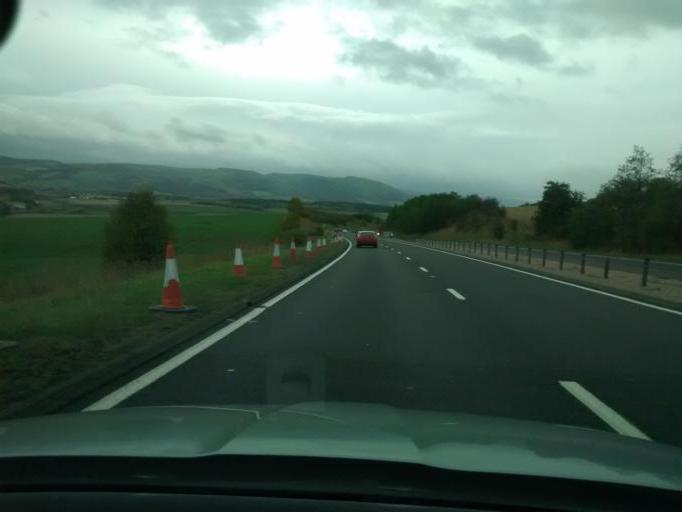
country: GB
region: Scotland
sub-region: Perth and Kinross
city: Methven
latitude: 56.3495
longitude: -3.5771
